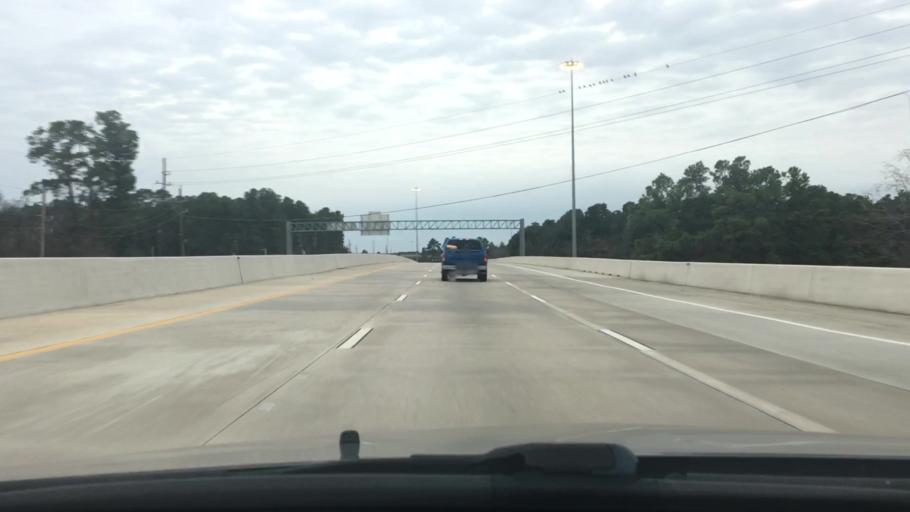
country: US
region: Texas
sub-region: Harris County
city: Spring
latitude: 30.0755
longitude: -95.4114
